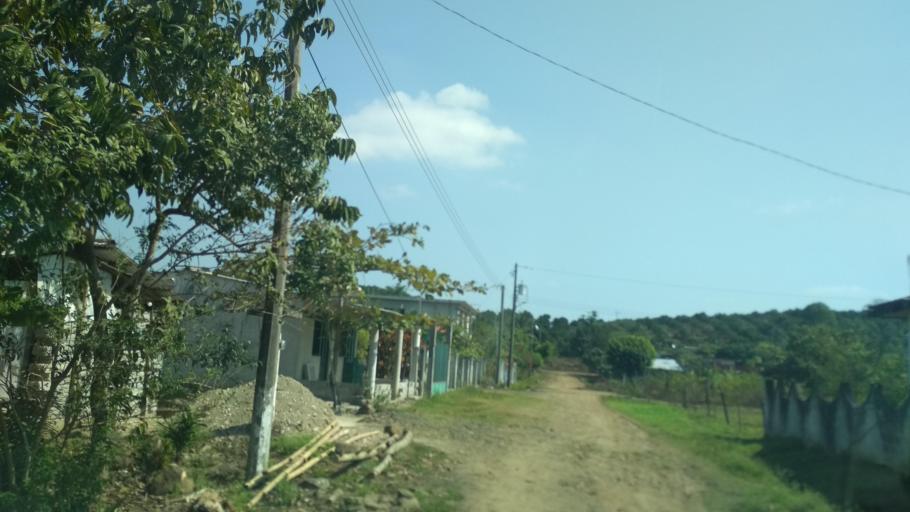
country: MX
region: Puebla
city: San Jose Acateno
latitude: 20.1764
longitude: -97.2295
